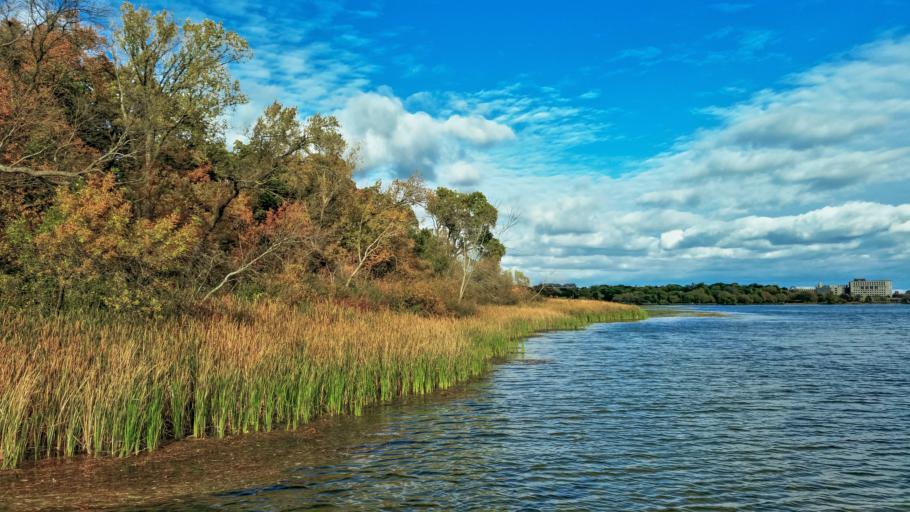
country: US
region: Wisconsin
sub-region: Dane County
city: Madison
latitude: 43.0556
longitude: -89.4227
